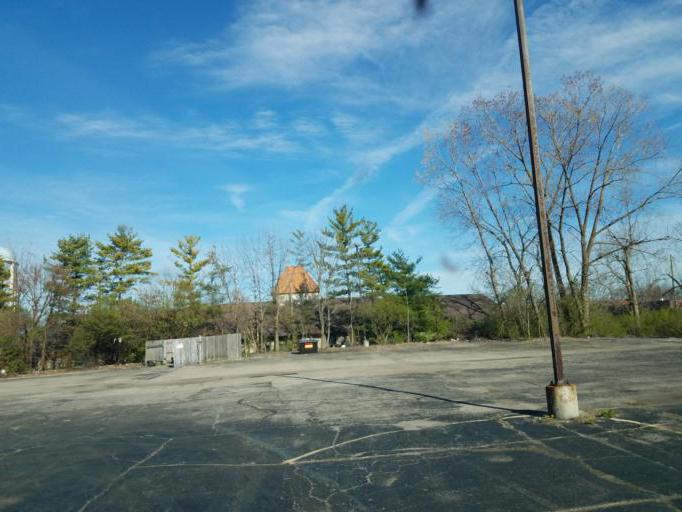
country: US
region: Ohio
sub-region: Franklin County
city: Upper Arlington
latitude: 40.0523
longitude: -83.0660
